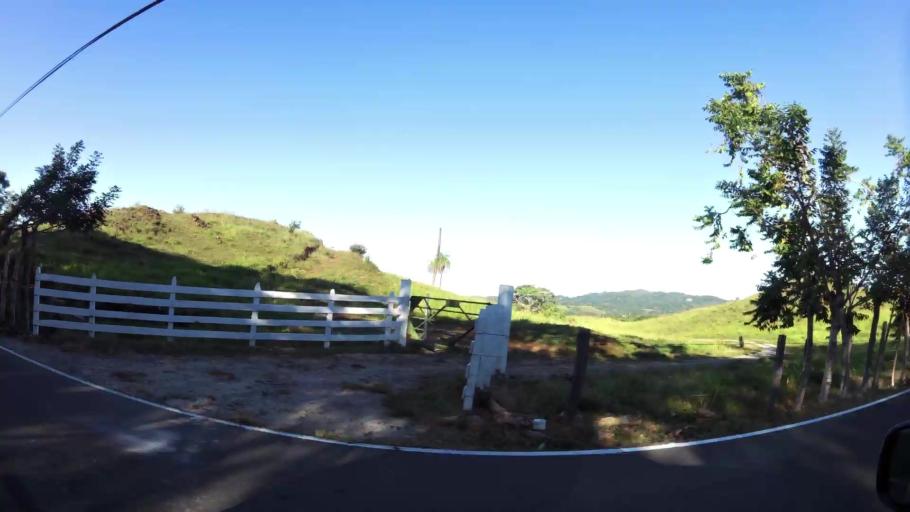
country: CR
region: Puntarenas
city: Miramar
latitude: 10.1478
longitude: -84.8521
